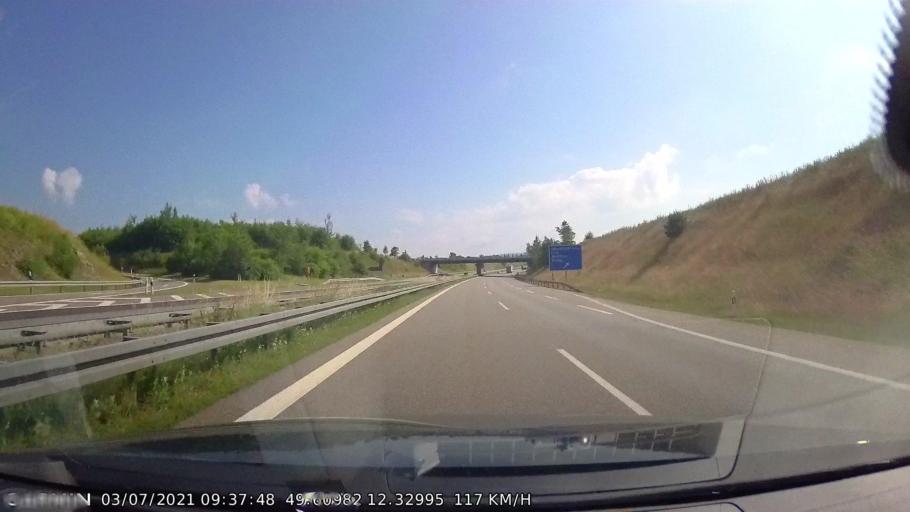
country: DE
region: Bavaria
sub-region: Upper Palatinate
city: Vohenstrauss
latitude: 49.6099
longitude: 12.3299
